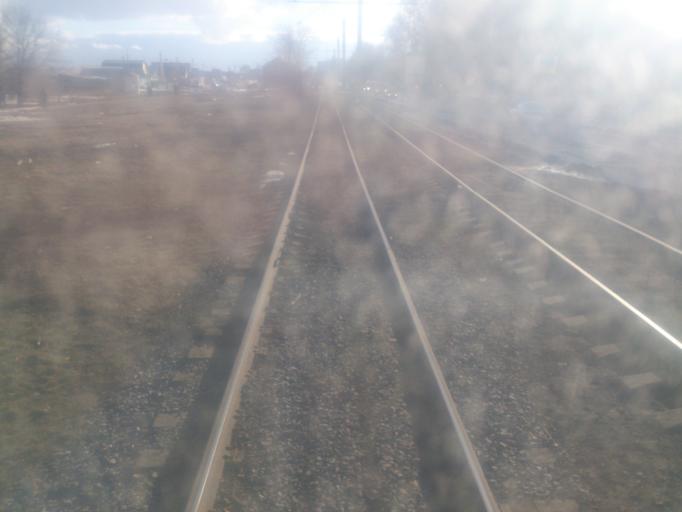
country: RU
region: Ulyanovsk
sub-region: Ulyanovskiy Rayon
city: Ulyanovsk
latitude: 54.2689
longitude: 48.2852
